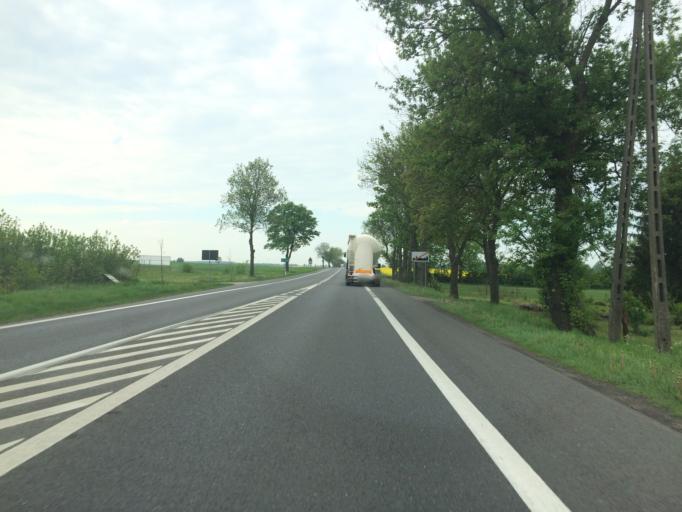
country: PL
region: Masovian Voivodeship
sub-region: Powiat mlawski
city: Wisniewo
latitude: 53.0587
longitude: 20.3464
